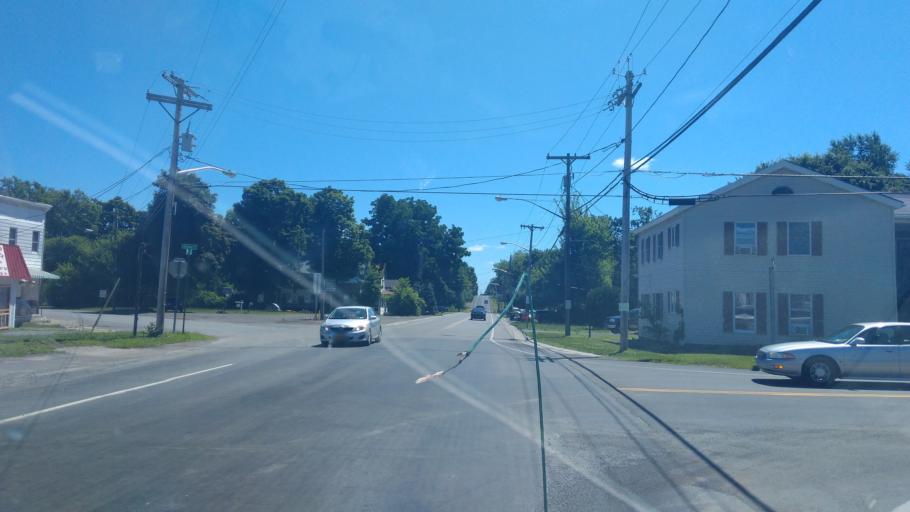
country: US
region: New York
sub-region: Wayne County
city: Sodus
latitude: 43.2111
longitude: -76.9806
